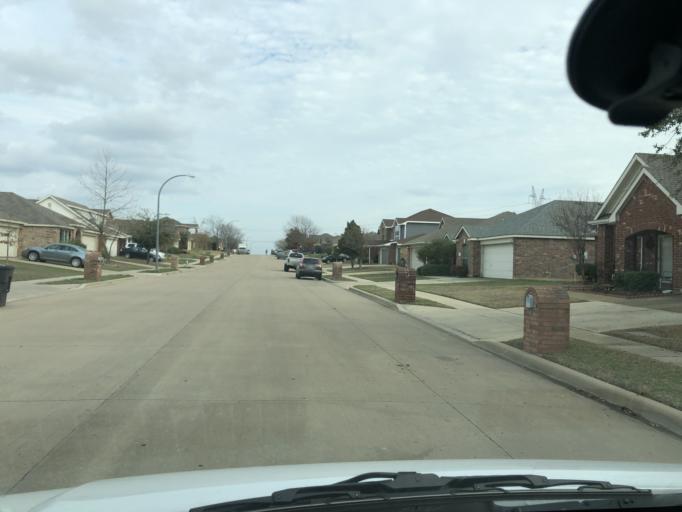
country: US
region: Texas
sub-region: Tarrant County
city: Saginaw
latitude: 32.9095
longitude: -97.3719
